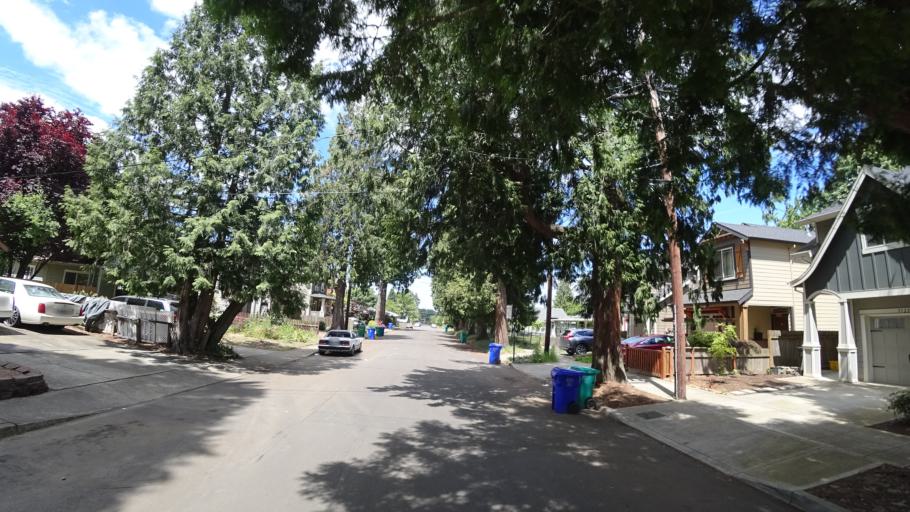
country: US
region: Washington
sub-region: Clark County
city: Vancouver
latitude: 45.5915
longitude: -122.7221
